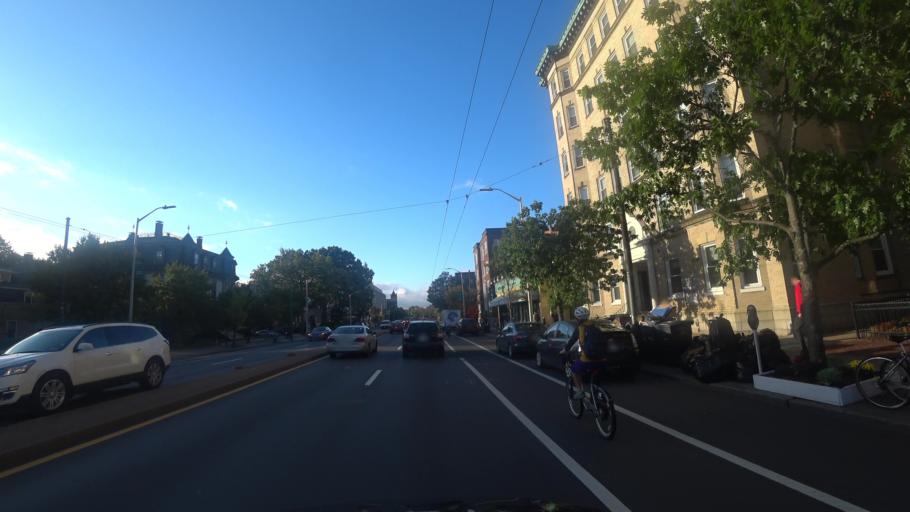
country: US
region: Massachusetts
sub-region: Middlesex County
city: Cambridge
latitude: 42.3818
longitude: -71.1198
